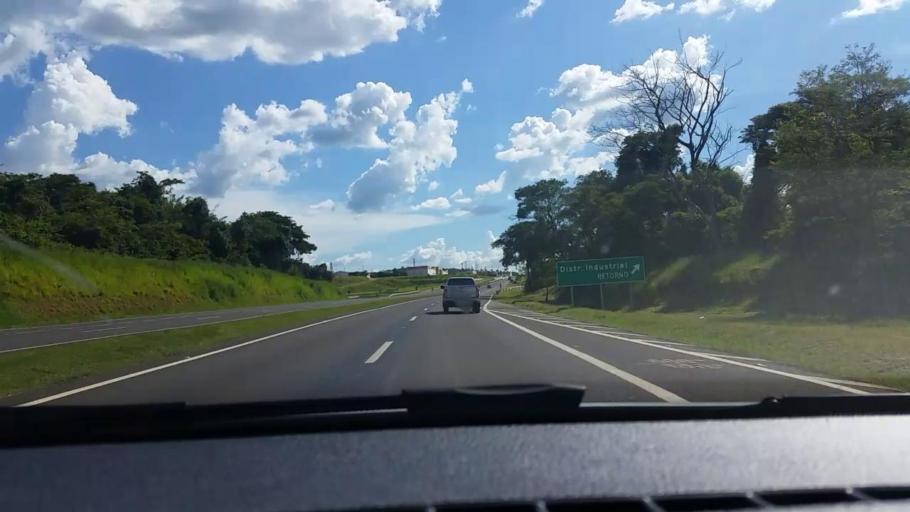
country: BR
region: Sao Paulo
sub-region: Bauru
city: Bauru
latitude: -22.4147
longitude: -49.1069
